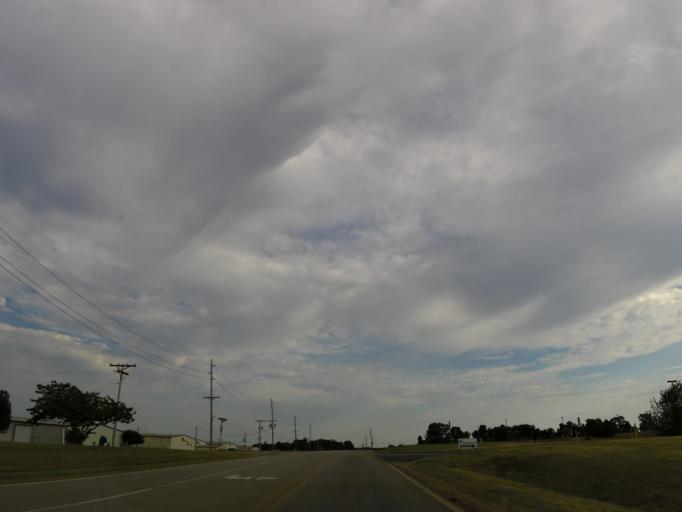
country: US
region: Alabama
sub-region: Morgan County
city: Trinity
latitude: 34.6304
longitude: -87.0384
